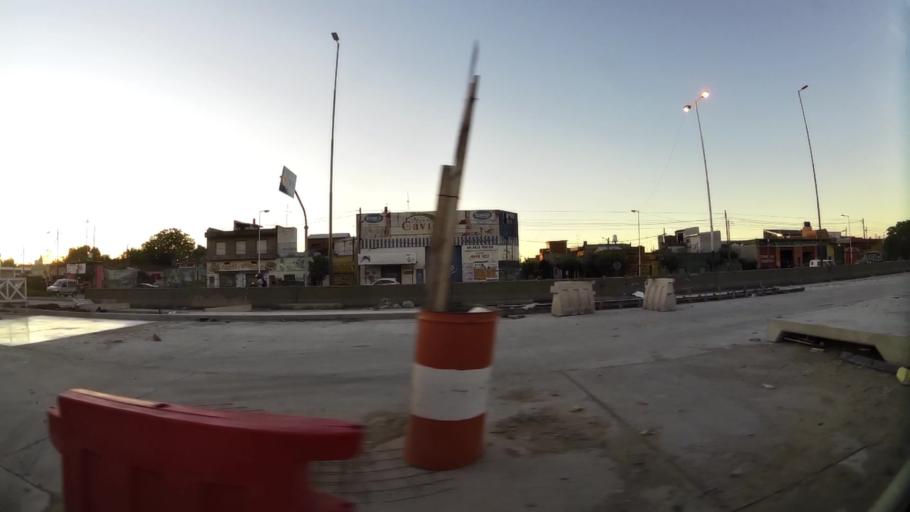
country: AR
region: Buenos Aires
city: Pontevedra
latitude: -34.7504
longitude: -58.6123
